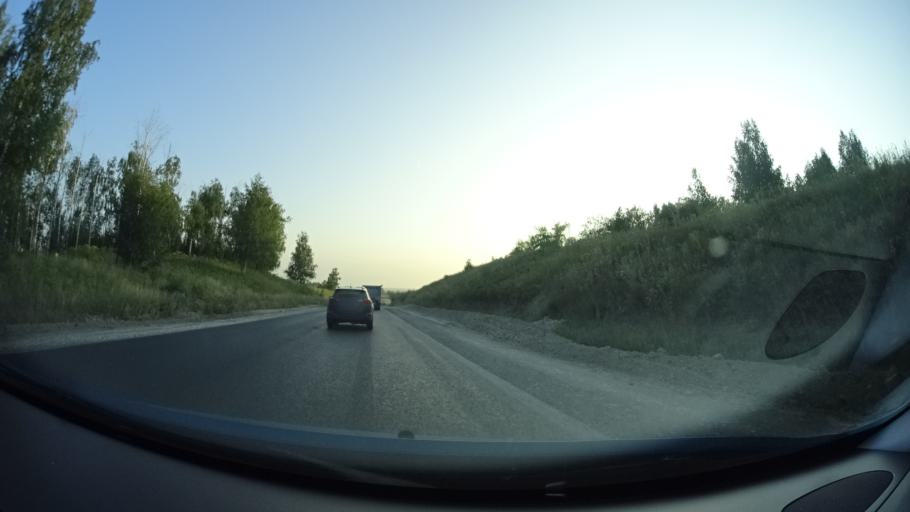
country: RU
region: Samara
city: Isakly
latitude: 53.9775
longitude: 51.4731
